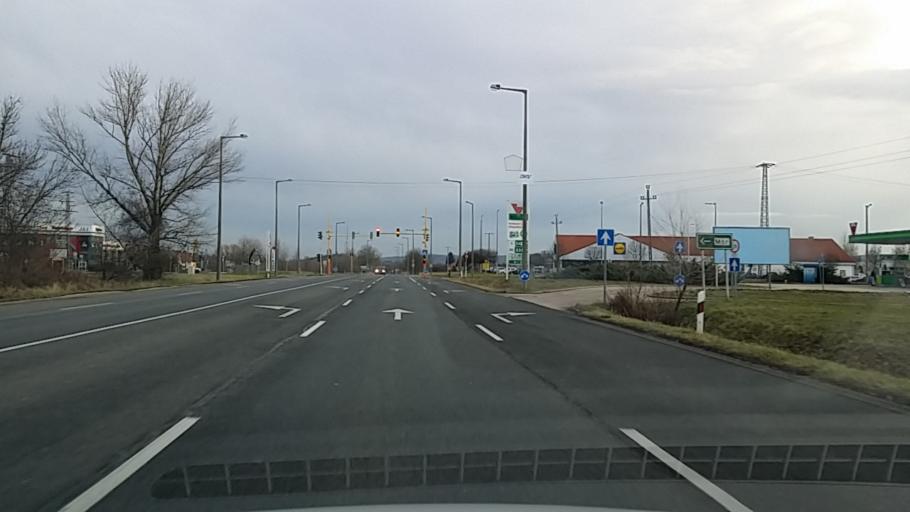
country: HU
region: Fejer
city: Mor
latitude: 47.3771
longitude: 18.1901
